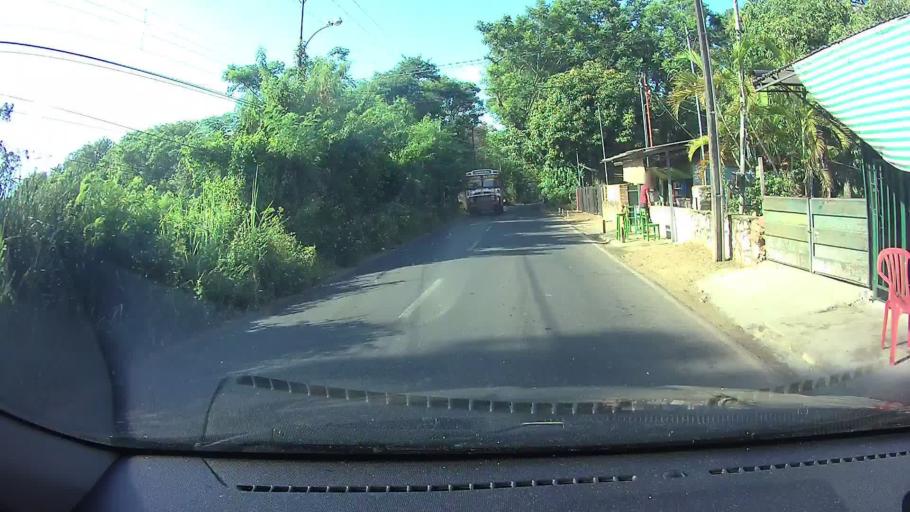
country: PY
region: Central
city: Fernando de la Mora
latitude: -25.2694
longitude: -57.5172
